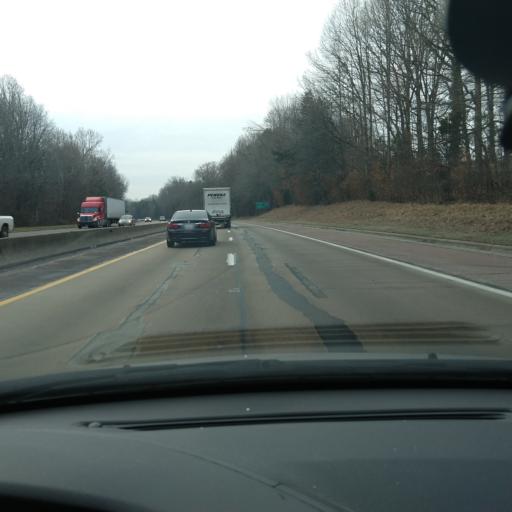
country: US
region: North Carolina
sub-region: Forsyth County
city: Winston-Salem
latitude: 36.0392
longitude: -80.2398
